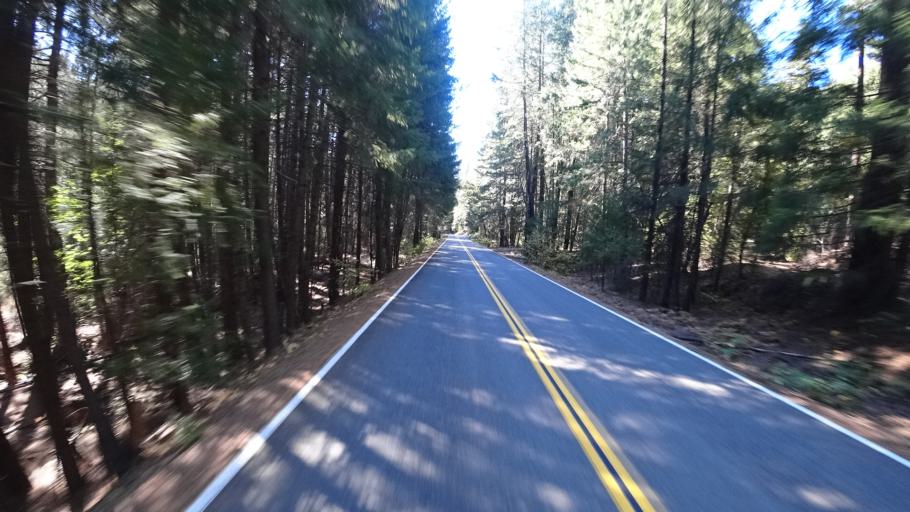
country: US
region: California
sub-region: Trinity County
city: Weaverville
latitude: 41.1991
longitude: -123.0709
